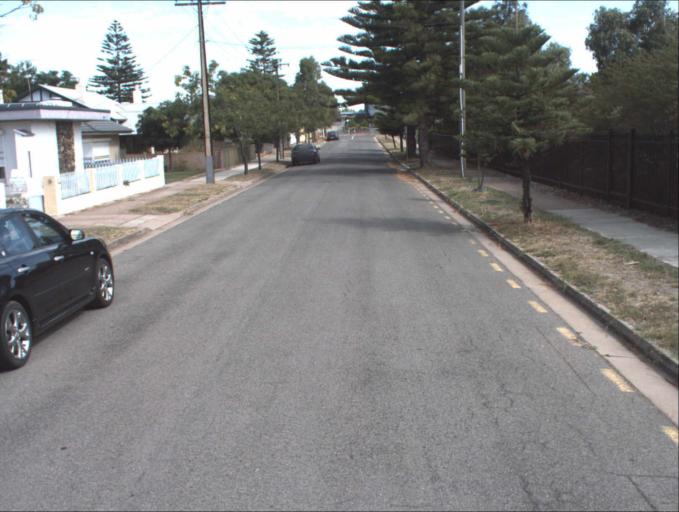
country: AU
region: South Australia
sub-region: Port Adelaide Enfield
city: Birkenhead
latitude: -34.8014
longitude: 138.4947
